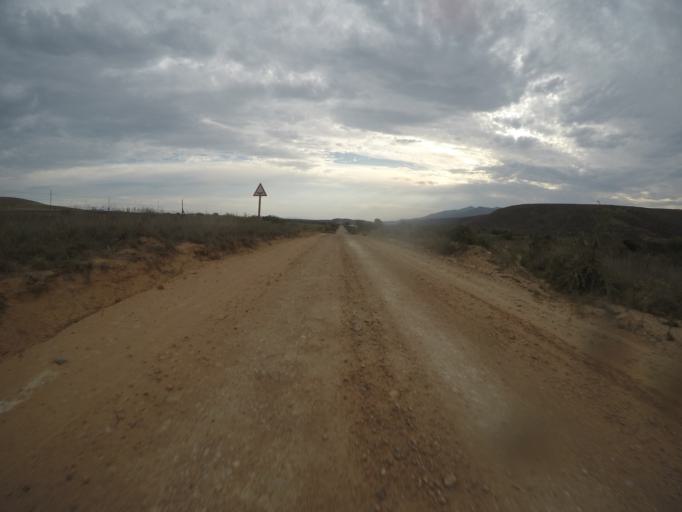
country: ZA
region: Eastern Cape
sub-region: Cacadu District Municipality
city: Willowmore
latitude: -33.4914
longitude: 23.5987
